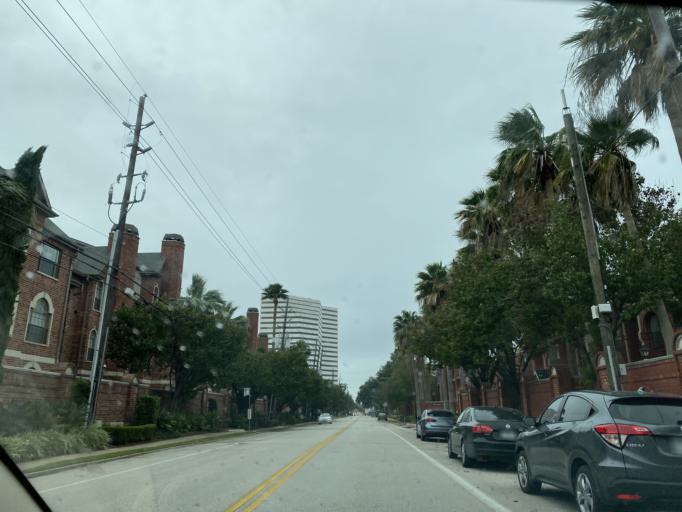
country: US
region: Texas
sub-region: Harris County
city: Hunters Creek Village
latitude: 29.7425
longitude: -95.4795
